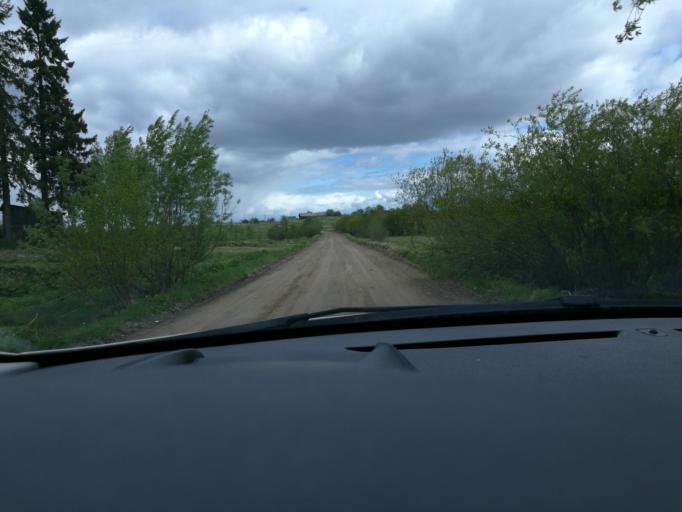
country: RU
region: Arkhangelskaya
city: Lukovetskiy
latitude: 64.2548
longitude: 41.7952
